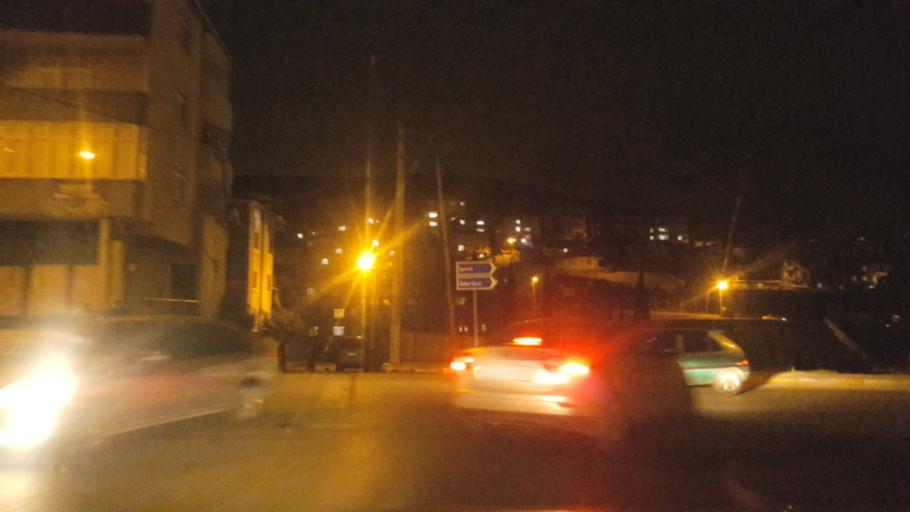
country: TR
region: Kocaeli
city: Tavsancil
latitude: 40.7836
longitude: 29.5434
